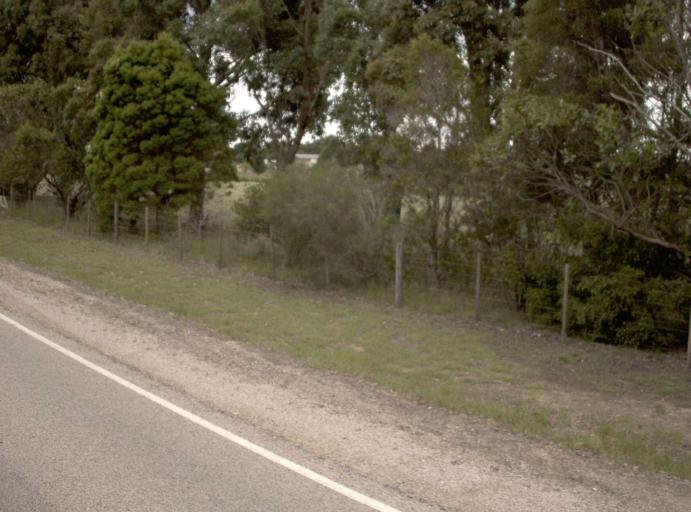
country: AU
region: Victoria
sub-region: East Gippsland
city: Bairnsdale
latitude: -37.8657
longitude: 147.5623
